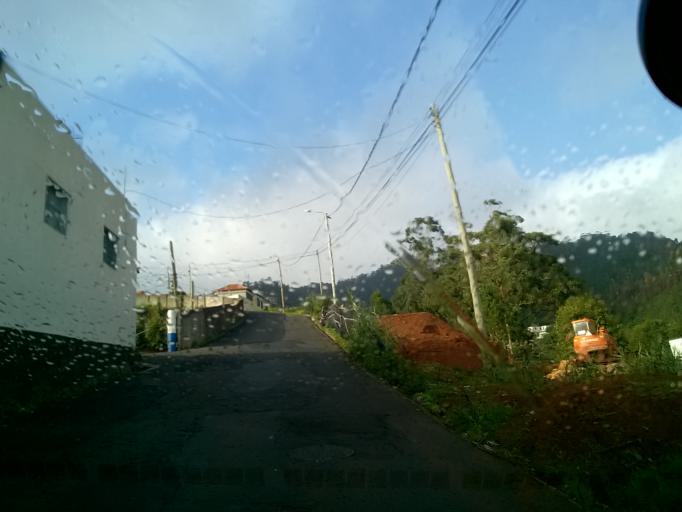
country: PT
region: Madeira
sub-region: Santa Cruz
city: Camacha
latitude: 32.6655
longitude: -16.8651
